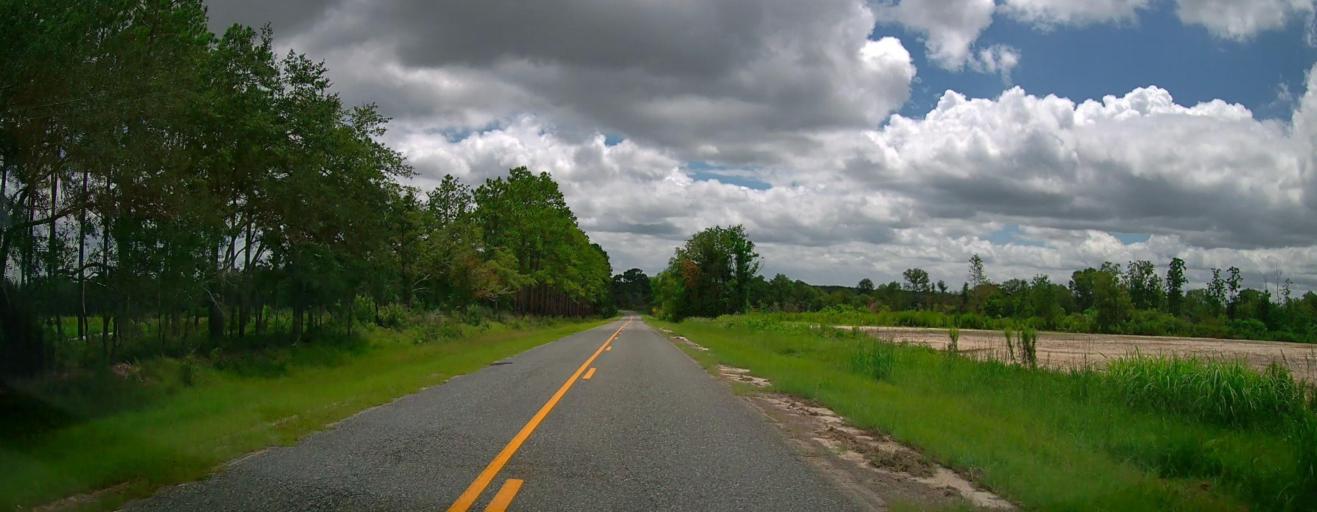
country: US
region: Georgia
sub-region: Turner County
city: Ashburn
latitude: 31.7105
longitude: -83.5055
